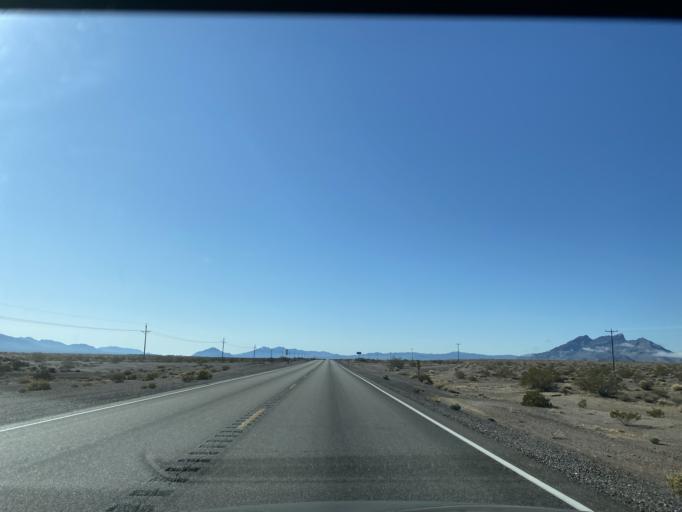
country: US
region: Nevada
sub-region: Nye County
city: Pahrump
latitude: 36.4679
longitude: -116.4217
